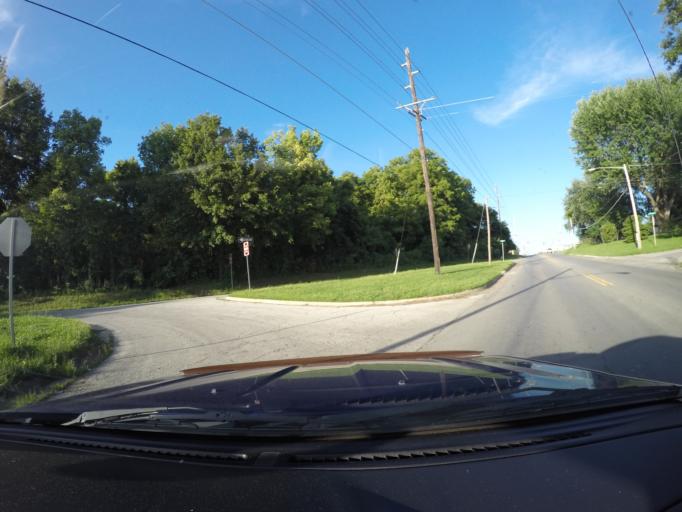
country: US
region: Missouri
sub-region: Platte County
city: Parkville
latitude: 39.1432
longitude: -94.7590
